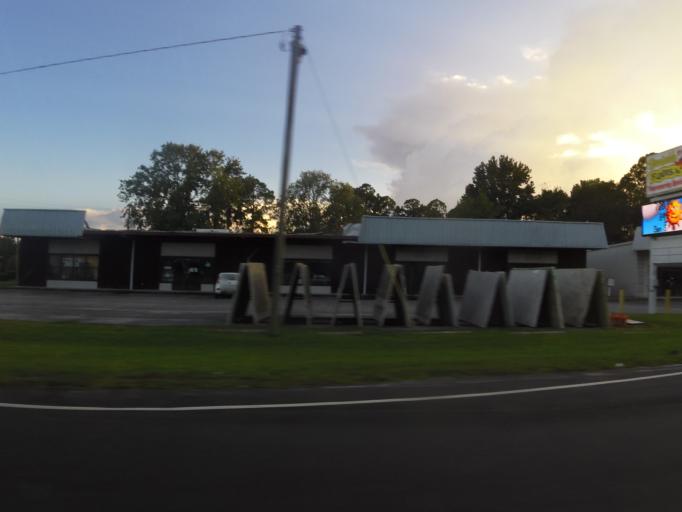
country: US
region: Georgia
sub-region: Camden County
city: Kingsland
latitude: 30.7995
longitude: -81.6783
